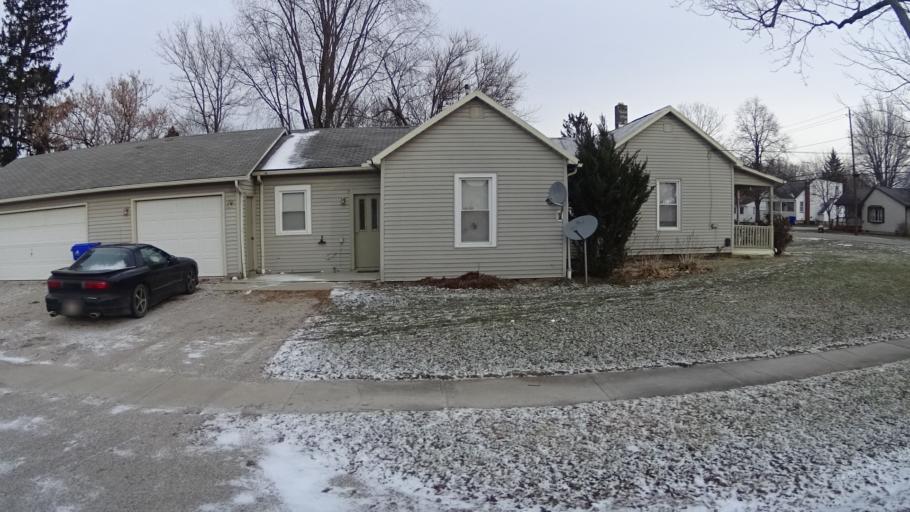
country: US
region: Ohio
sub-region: Lorain County
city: Lagrange
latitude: 41.2395
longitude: -82.1183
